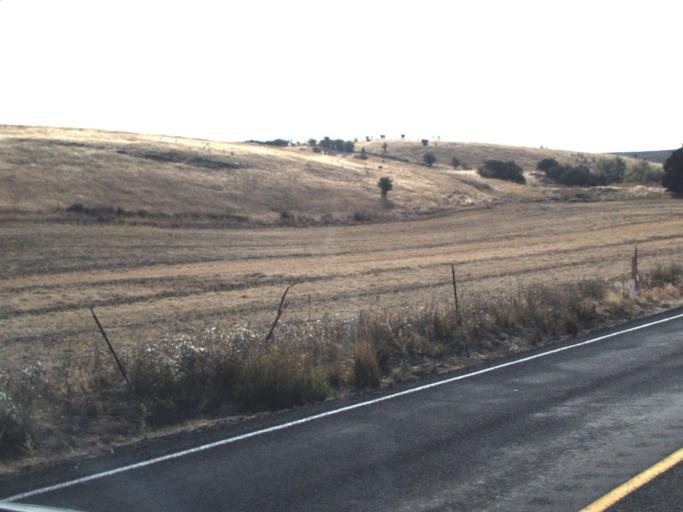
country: US
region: Idaho
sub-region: Benewah County
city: Plummer
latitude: 47.2574
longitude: -117.1305
